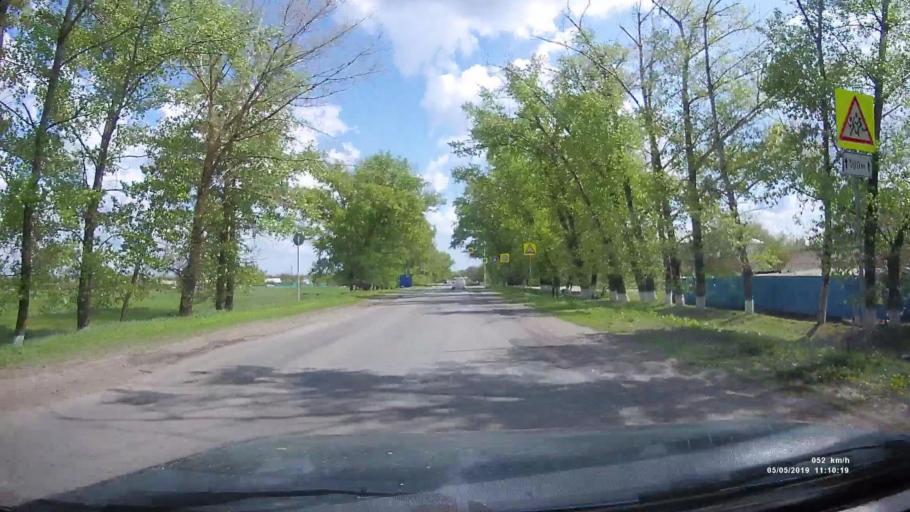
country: RU
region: Rostov
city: Ust'-Donetskiy
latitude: 47.7436
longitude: 40.9364
